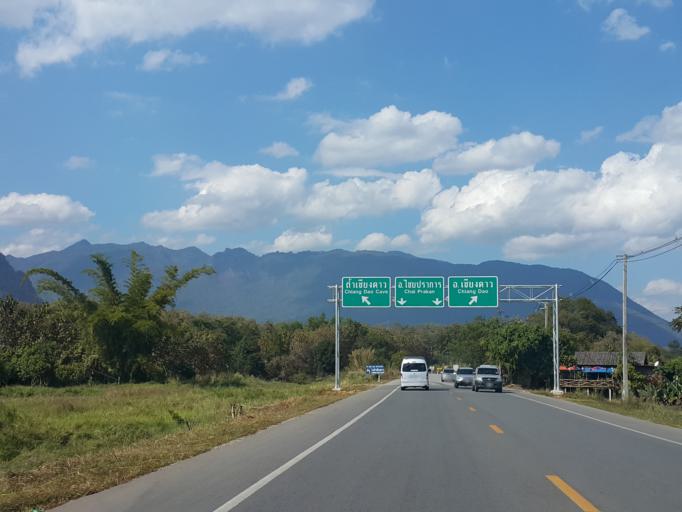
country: TH
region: Chiang Mai
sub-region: Amphoe Chiang Dao
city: Chiang Dao
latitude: 19.3726
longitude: 98.9476
